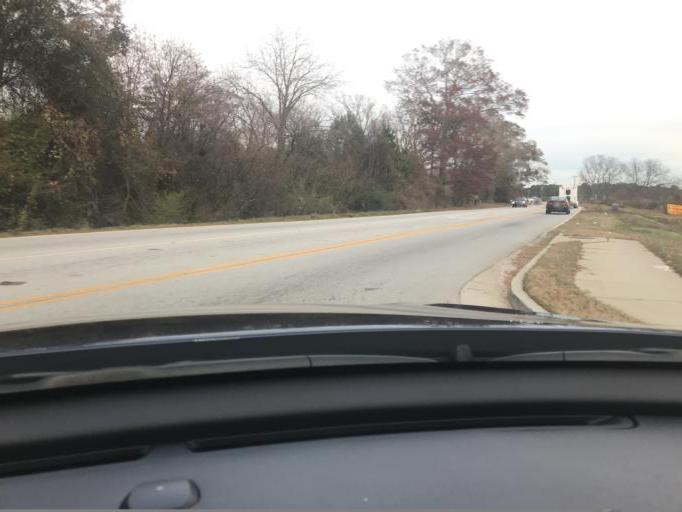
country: US
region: Georgia
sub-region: Newton County
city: Oakwood
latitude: 33.5782
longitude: -83.9585
